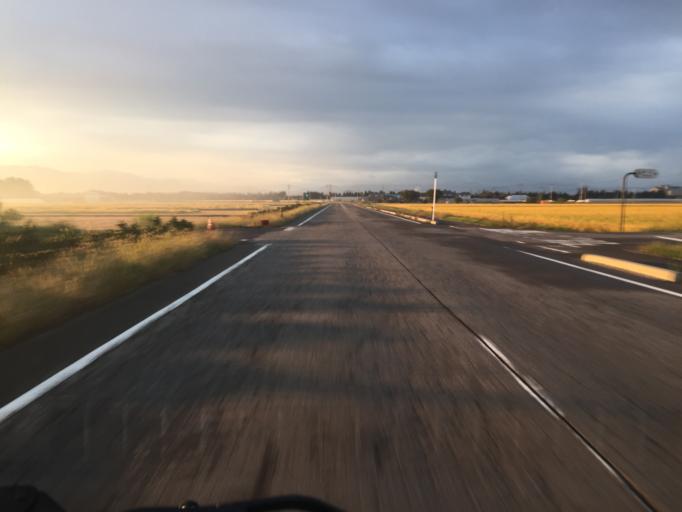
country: JP
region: Fukushima
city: Kitakata
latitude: 37.5408
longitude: 139.8989
